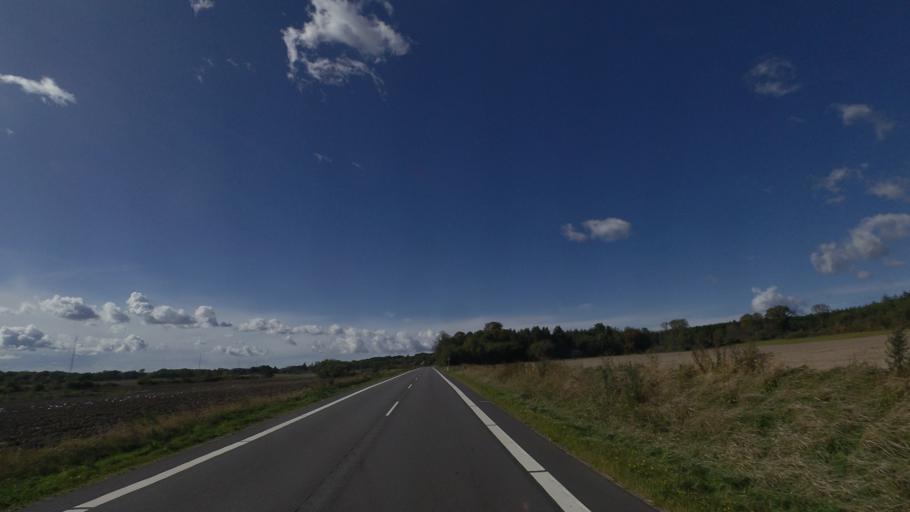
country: DK
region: Capital Region
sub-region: Bornholm Kommune
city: Nexo
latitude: 55.0622
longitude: 15.0338
